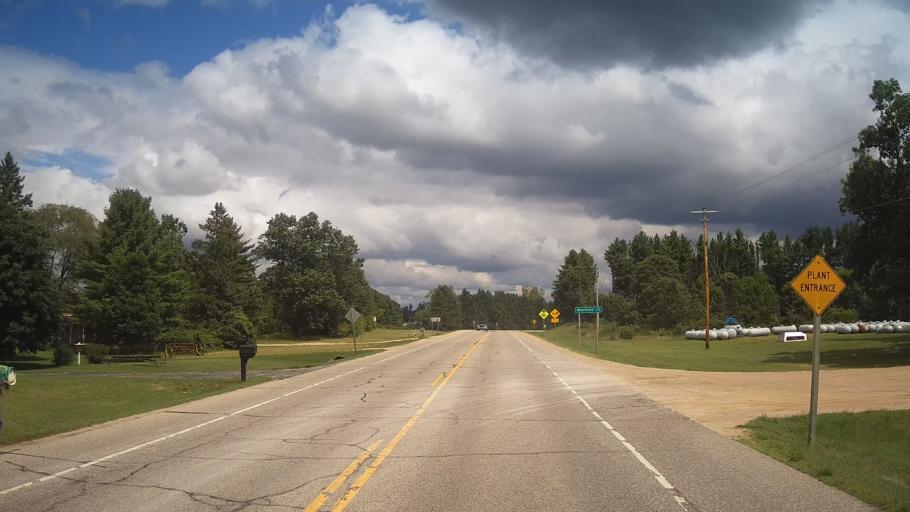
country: US
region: Wisconsin
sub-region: Marquette County
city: Westfield
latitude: 44.0374
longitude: -89.5140
